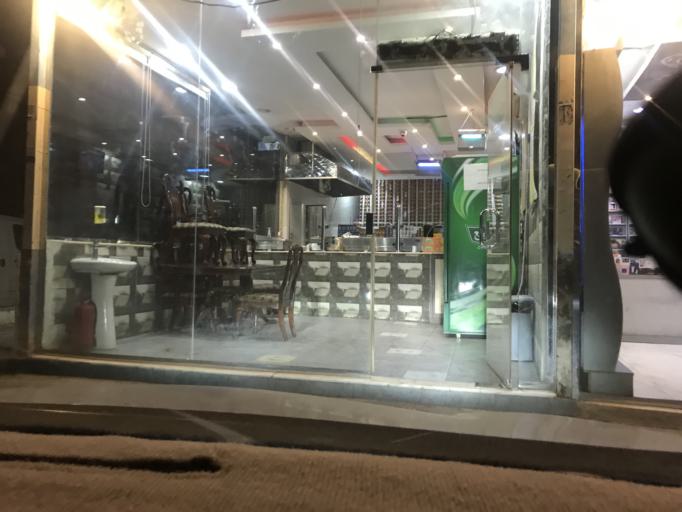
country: SA
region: Ar Riyad
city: Riyadh
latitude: 24.8509
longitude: 46.6029
